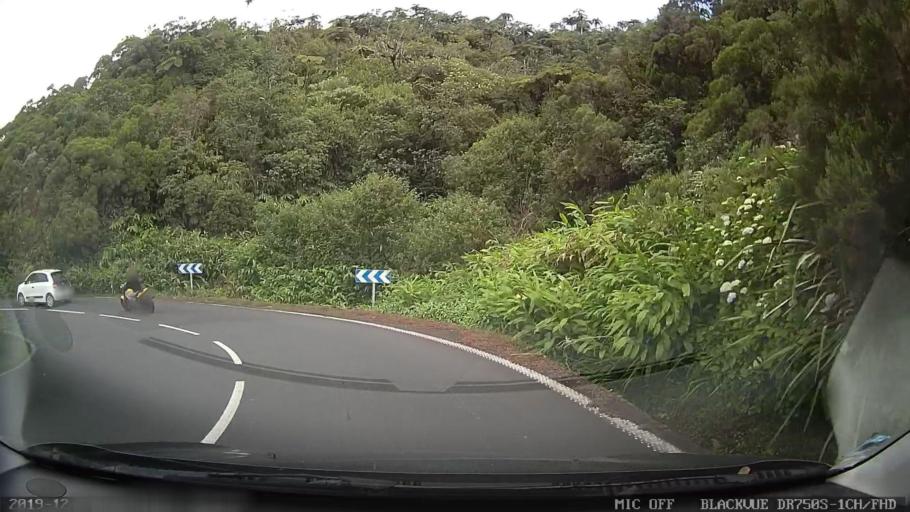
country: RE
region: Reunion
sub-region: Reunion
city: Cilaos
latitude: -21.1608
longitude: 55.5958
